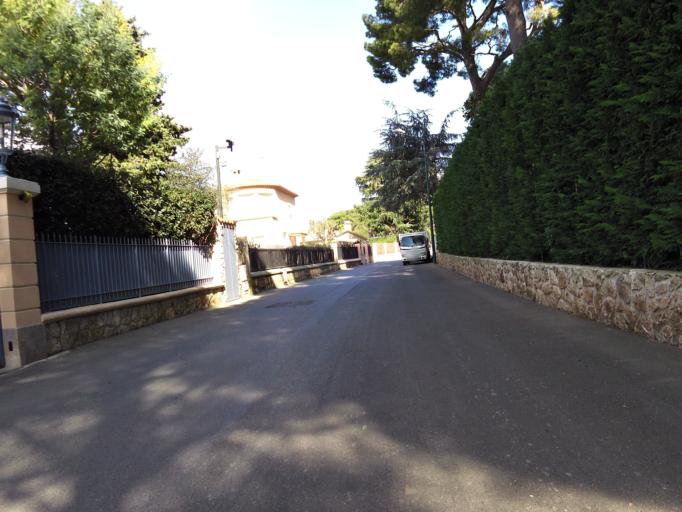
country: FR
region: Provence-Alpes-Cote d'Azur
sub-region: Departement des Alpes-Maritimes
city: Saint-Jean-Cap-Ferrat
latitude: 43.6903
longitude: 7.3221
